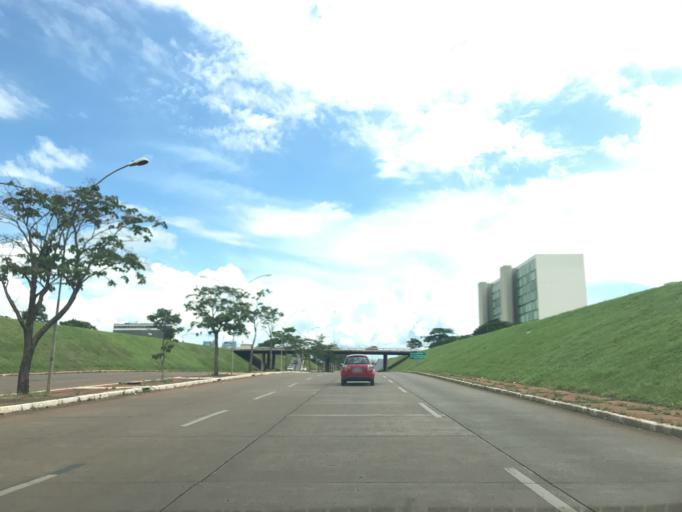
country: BR
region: Federal District
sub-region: Brasilia
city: Brasilia
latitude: -15.7967
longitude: -47.8762
